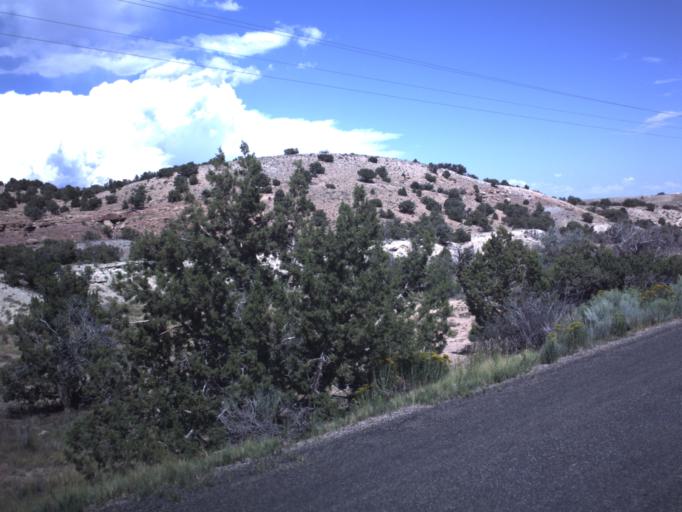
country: US
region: Utah
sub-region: Duchesne County
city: Duchesne
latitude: 40.1771
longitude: -110.4473
